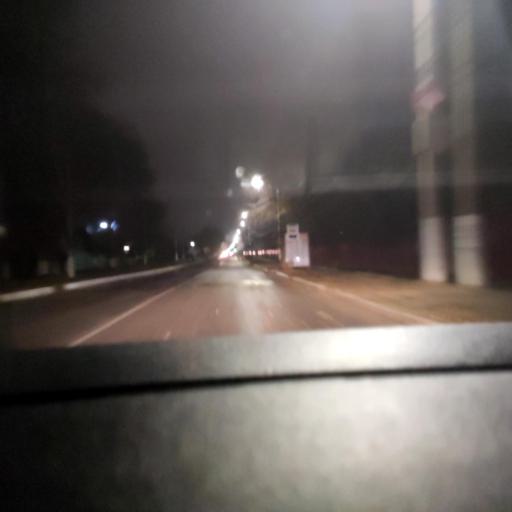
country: RU
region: Voronezj
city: Semiluki
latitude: 51.6921
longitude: 39.0346
